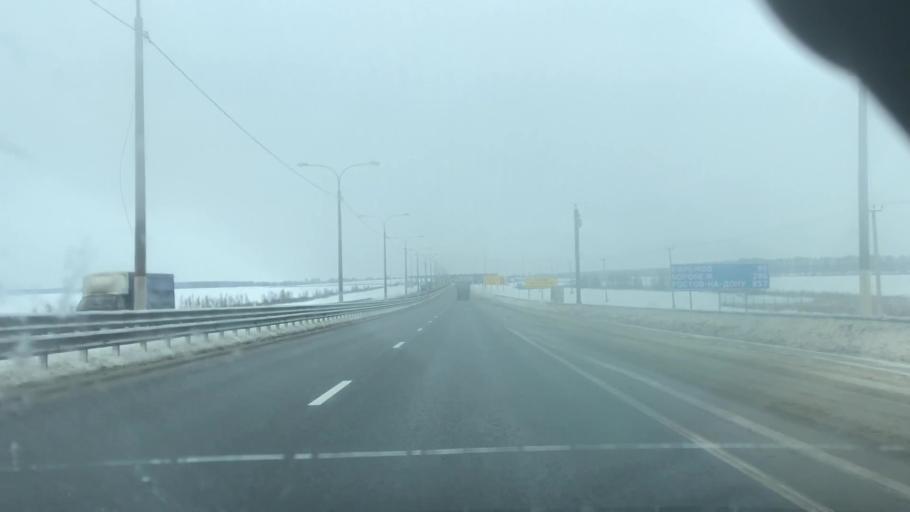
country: RU
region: Tula
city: Dubovka
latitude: 53.8855
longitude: 38.0519
